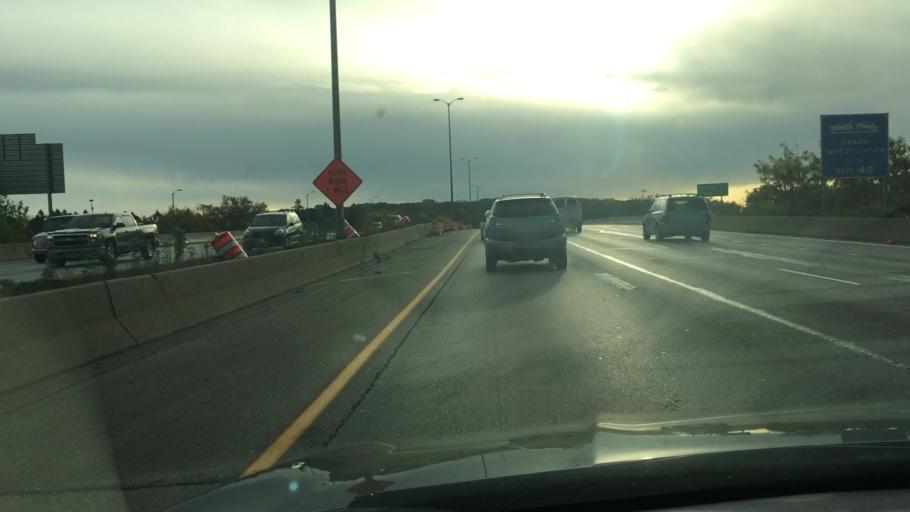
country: US
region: Wisconsin
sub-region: Waukesha County
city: Elm Grove
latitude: 43.0558
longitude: -88.0486
